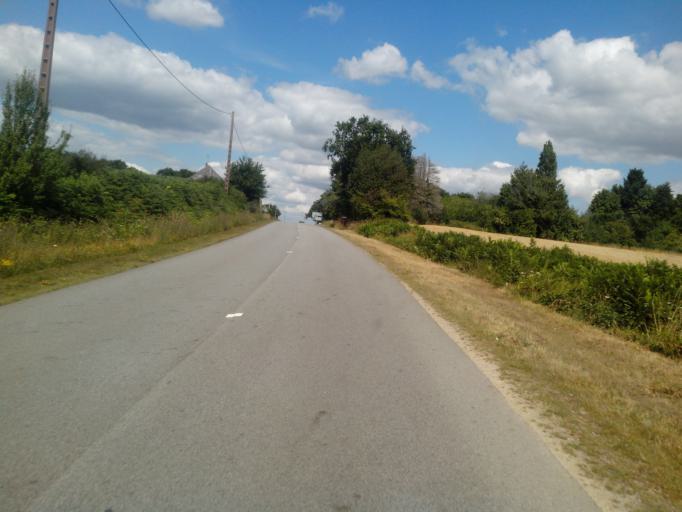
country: FR
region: Brittany
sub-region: Departement du Morbihan
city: Guegon
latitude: 47.9442
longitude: -2.5577
